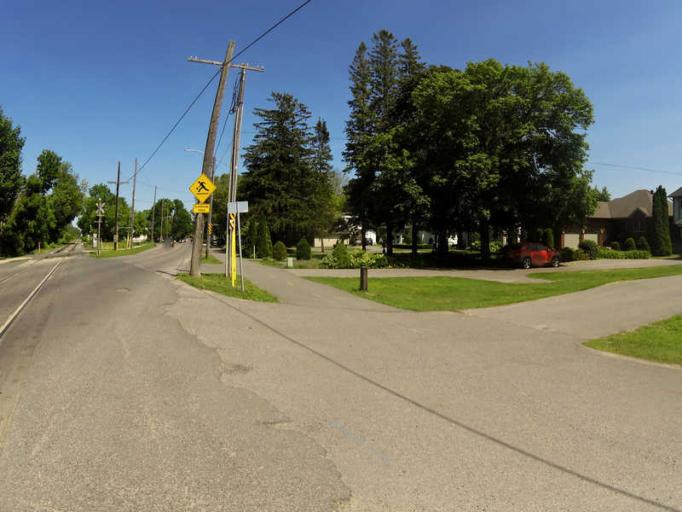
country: CA
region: Ontario
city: Peterborough
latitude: 44.3007
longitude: -78.3107
